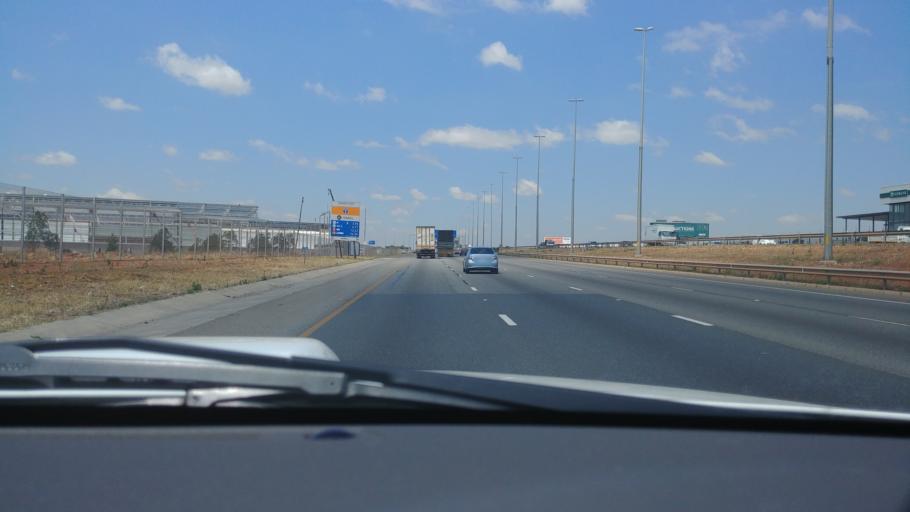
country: ZA
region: Gauteng
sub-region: Ekurhuleni Metropolitan Municipality
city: Tembisa
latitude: -26.0216
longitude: 28.2610
